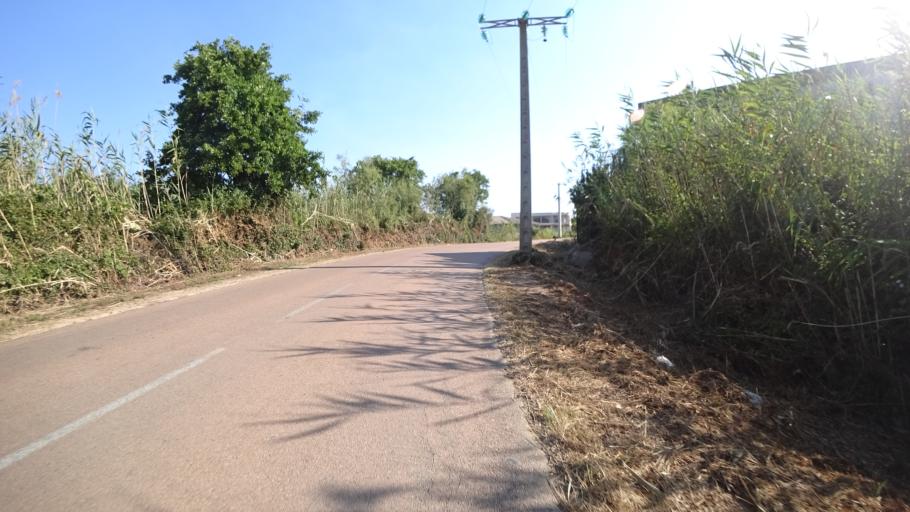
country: FR
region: Corsica
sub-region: Departement de la Corse-du-Sud
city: Porto-Vecchio
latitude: 41.6232
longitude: 9.3341
